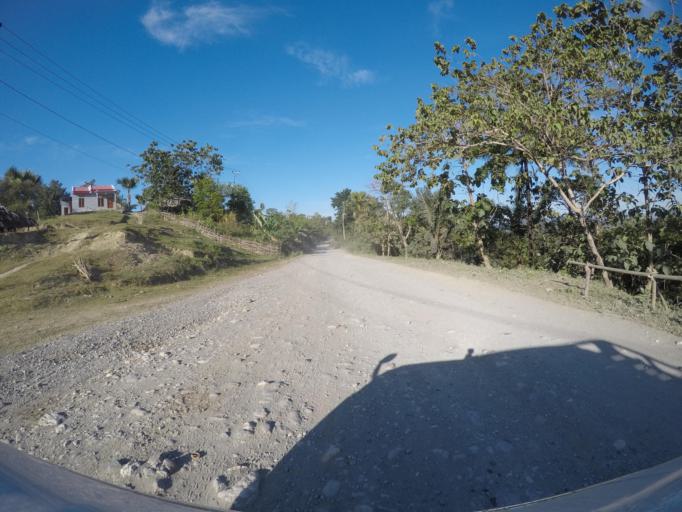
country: TL
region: Viqueque
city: Viqueque
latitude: -8.8666
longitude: 126.3330
